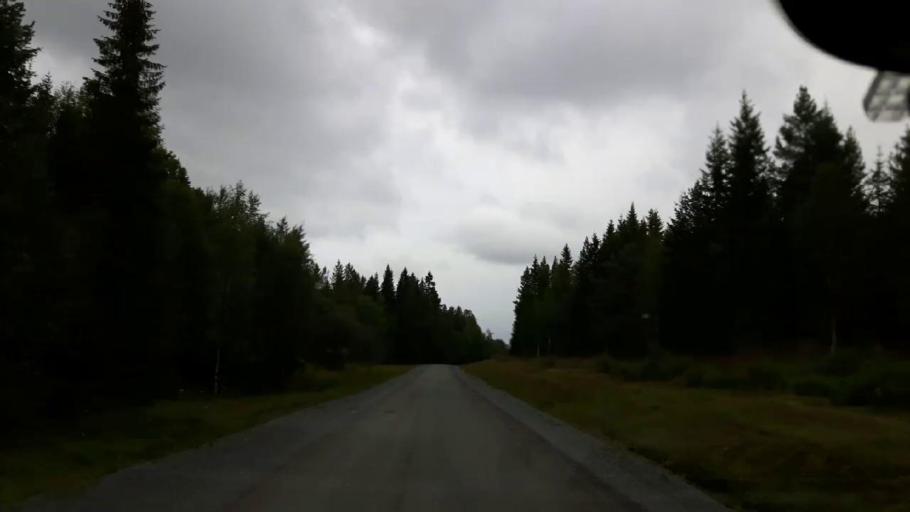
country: SE
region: Jaemtland
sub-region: OEstersunds Kommun
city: Ostersund
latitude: 63.0699
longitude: 14.5530
